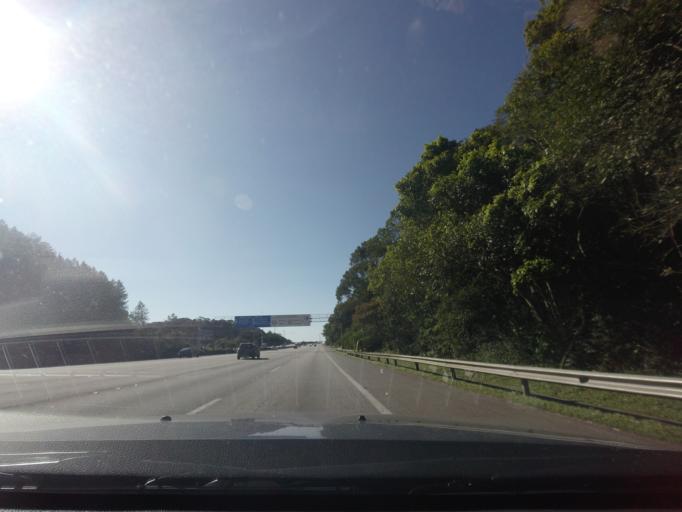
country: BR
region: Sao Paulo
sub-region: Sao Bernardo Do Campo
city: Sao Bernardo do Campo
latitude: -23.8278
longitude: -46.5805
